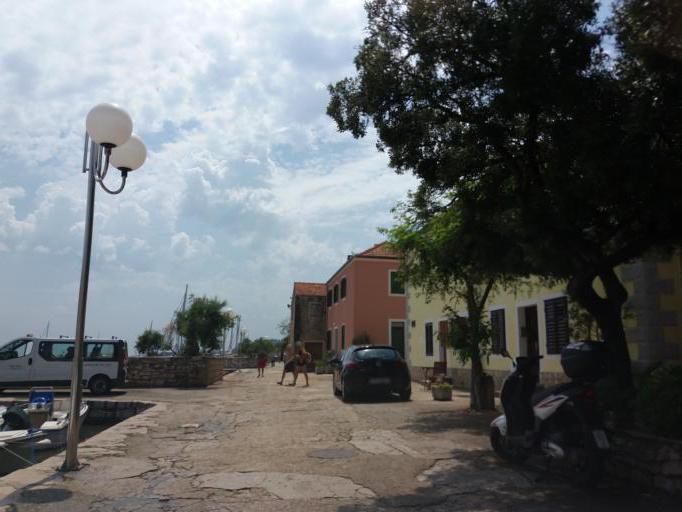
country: HR
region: Zadarska
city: Sali
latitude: 43.9372
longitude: 15.1650
